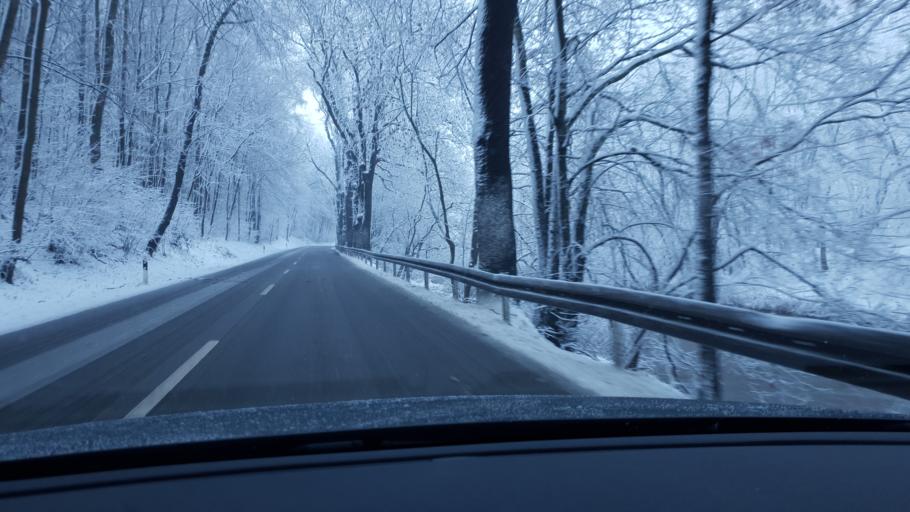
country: DE
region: Saxony
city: Claussnitz
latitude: 50.9164
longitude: 12.8710
